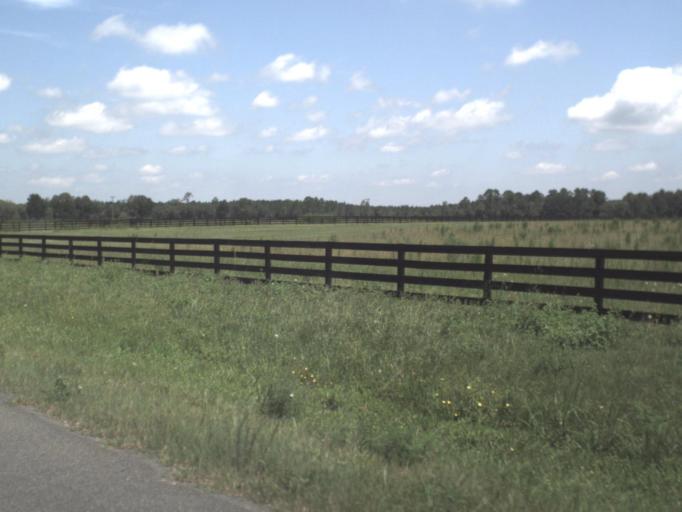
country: US
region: Florida
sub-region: Clay County
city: Green Cove Springs
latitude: 29.9796
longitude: -81.5526
